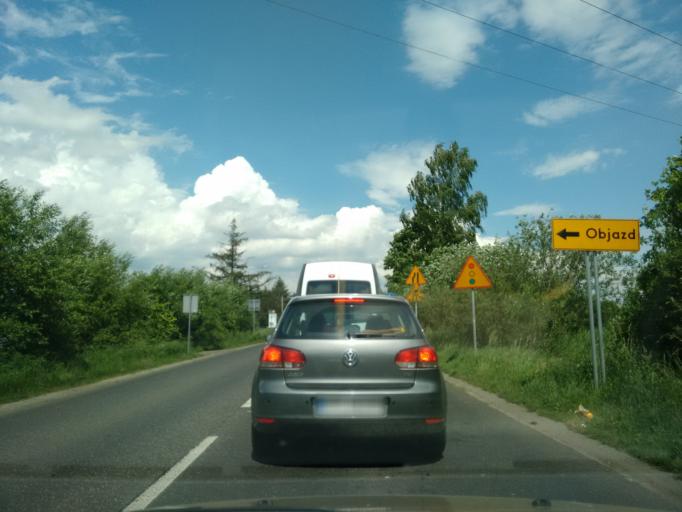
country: PL
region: Silesian Voivodeship
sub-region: Powiat cieszynski
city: Pruchna
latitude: 49.8625
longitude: 18.6804
